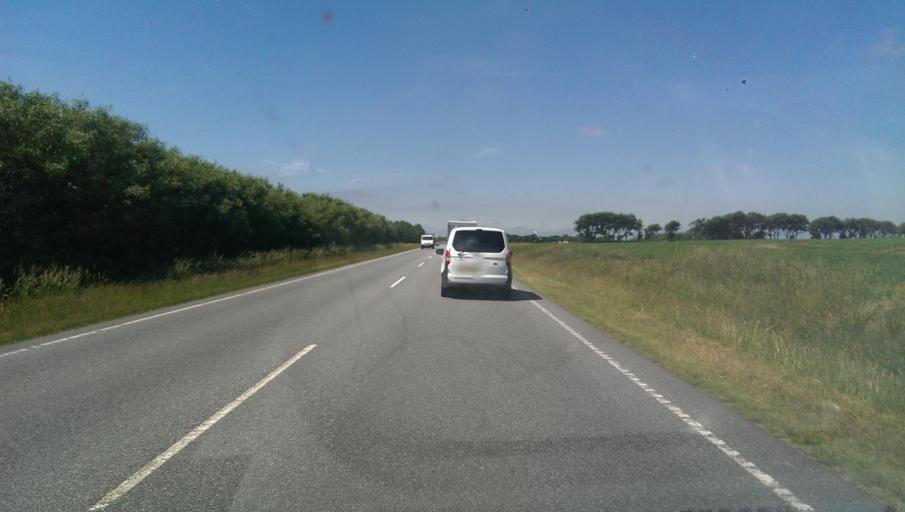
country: DK
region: South Denmark
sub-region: Esbjerg Kommune
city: Esbjerg
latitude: 55.5314
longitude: 8.4293
